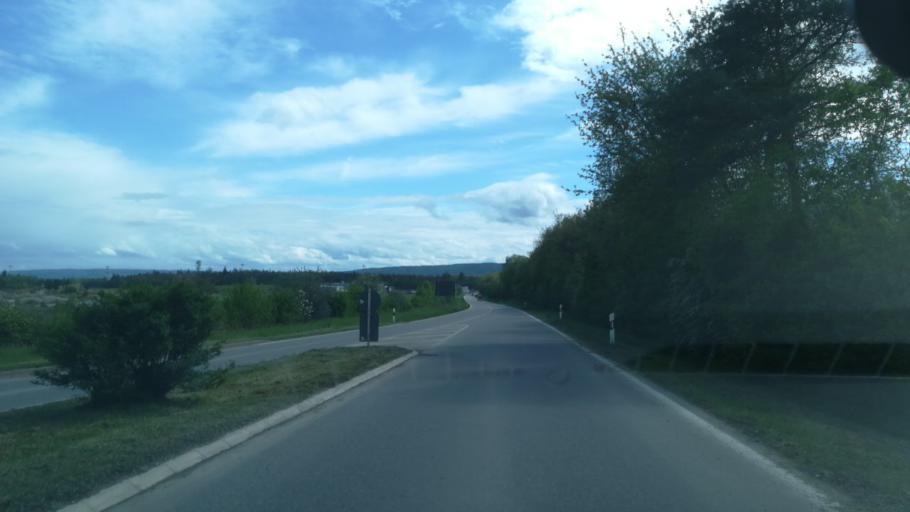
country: DE
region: Baden-Wuerttemberg
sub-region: Freiburg Region
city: Steisslingen
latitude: 47.7835
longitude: 8.9157
